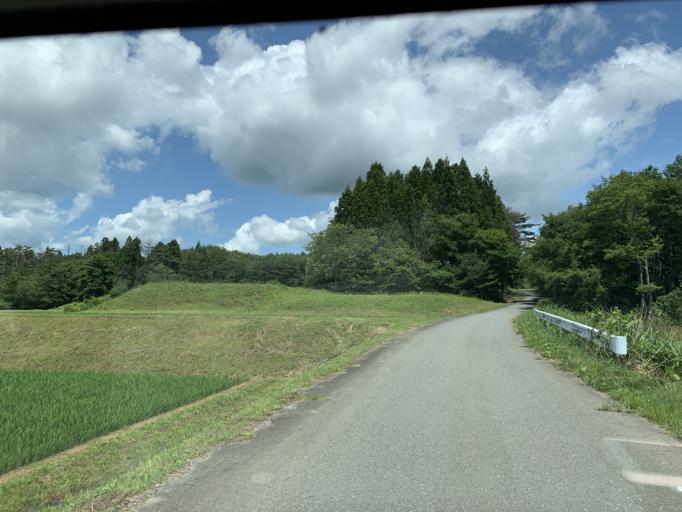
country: JP
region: Iwate
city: Ichinoseki
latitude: 38.9242
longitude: 141.0492
